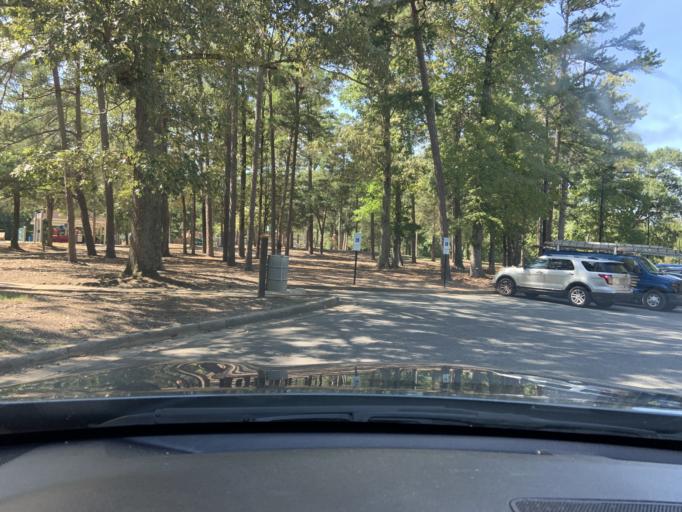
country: US
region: North Carolina
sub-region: Mecklenburg County
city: Pineville
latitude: 35.1474
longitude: -80.8505
